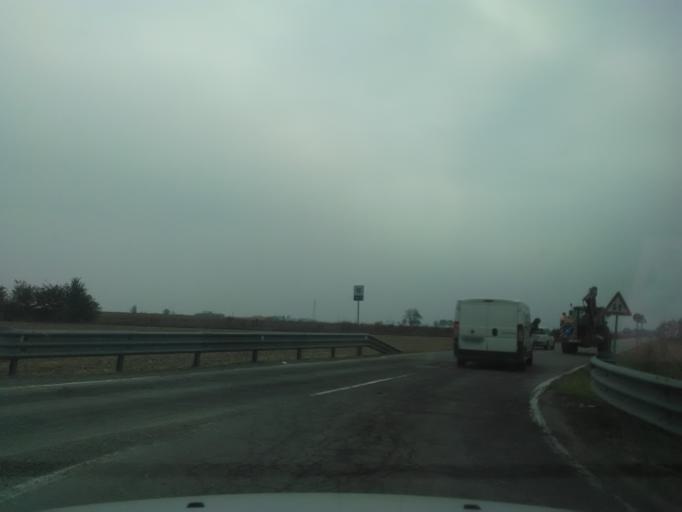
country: IT
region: Piedmont
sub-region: Provincia di Vercelli
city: Livorno Ferraris
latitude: 45.2889
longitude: 8.0939
